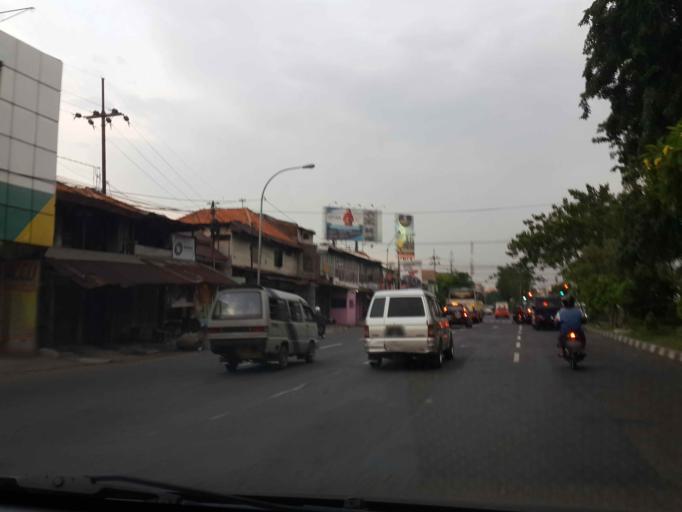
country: ID
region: East Java
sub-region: Kota Surabaya
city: Surabaya
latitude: -7.2452
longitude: 112.7201
